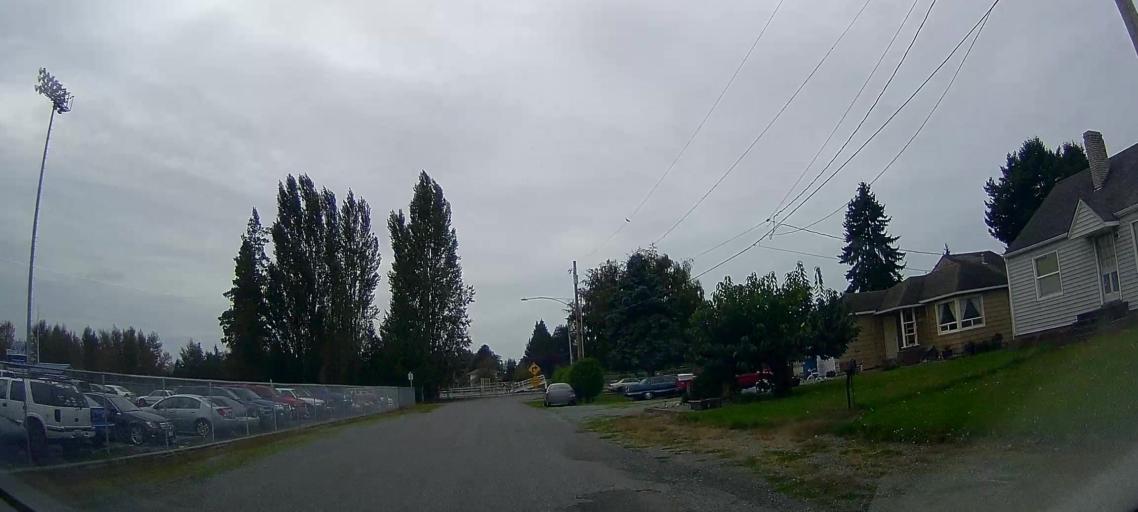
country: US
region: Washington
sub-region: Skagit County
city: Sedro-Woolley
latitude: 48.5007
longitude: -122.2392
